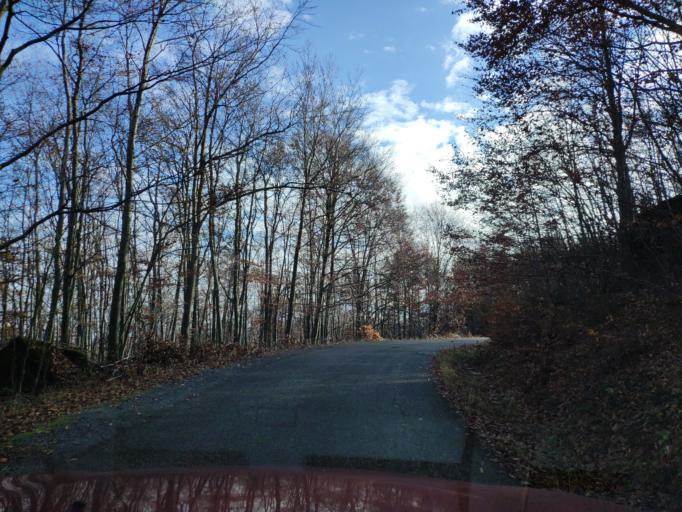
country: SK
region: Kosicky
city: Secovce
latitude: 48.6084
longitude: 21.4572
